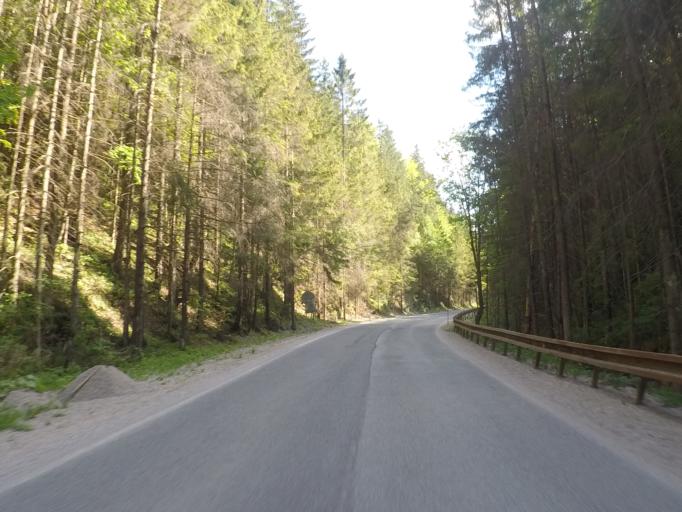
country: SK
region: Kosicky
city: Dobsina
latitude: 48.8631
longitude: 20.3505
